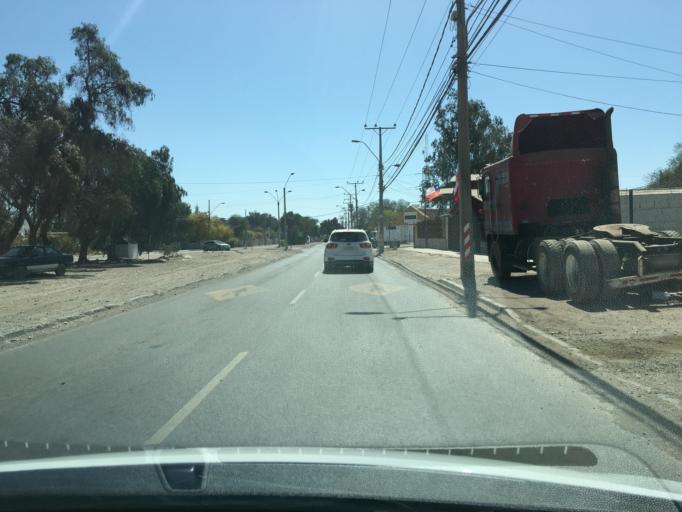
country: CL
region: Atacama
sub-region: Provincia de Copiapo
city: Copiapo
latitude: -27.4130
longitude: -70.2818
